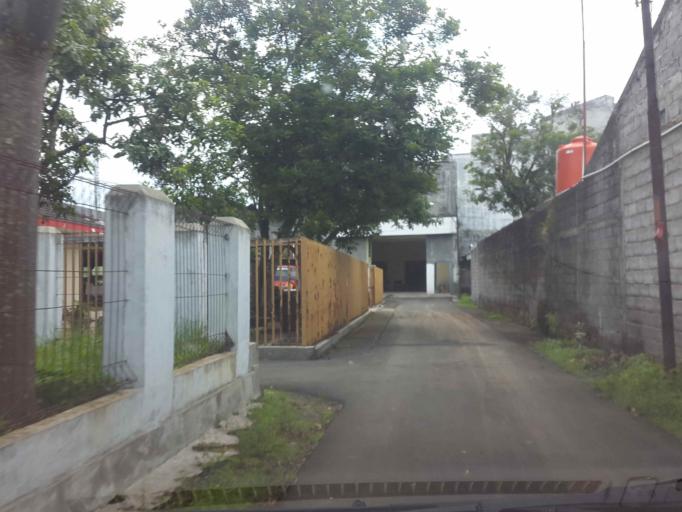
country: ID
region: Central Java
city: Salatiga
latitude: -7.3603
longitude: 110.5140
